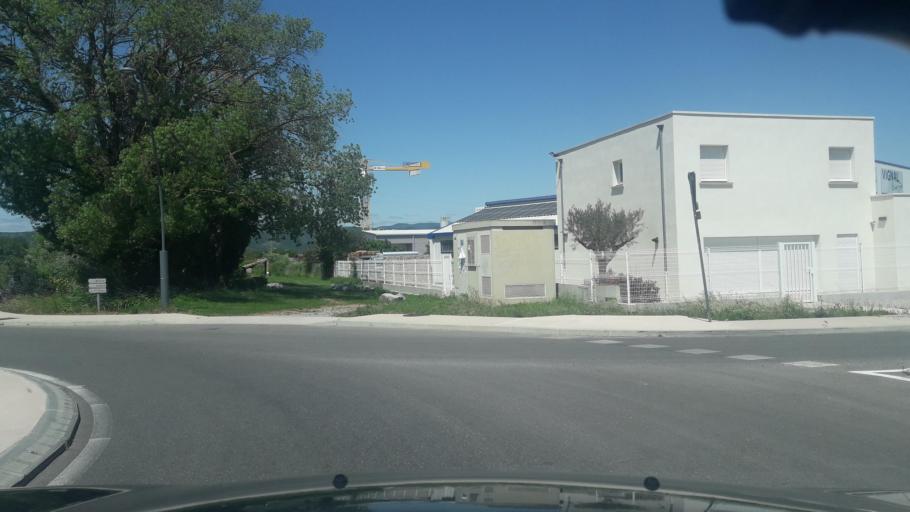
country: FR
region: Rhone-Alpes
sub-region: Departement de la Drome
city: Livron-sur-Drome
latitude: 44.7800
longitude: 4.8264
